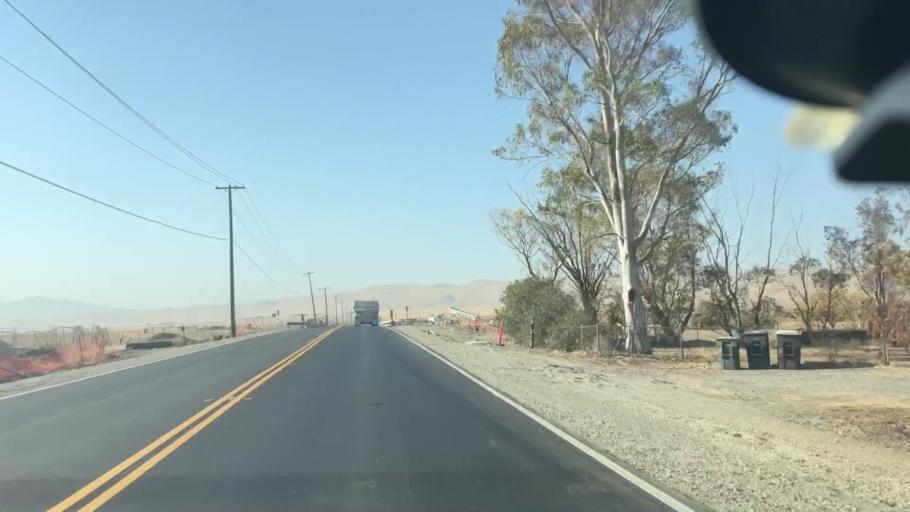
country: US
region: California
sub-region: San Joaquin County
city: Tracy
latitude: 37.6813
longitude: -121.4528
